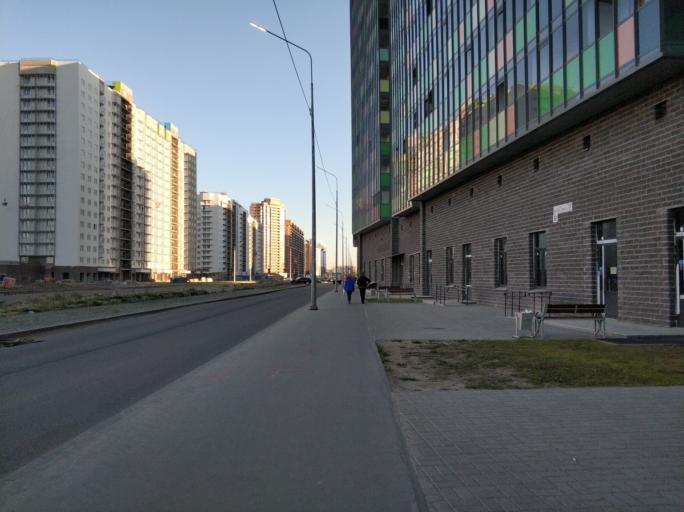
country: RU
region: Leningrad
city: Murino
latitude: 60.0618
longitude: 30.4318
